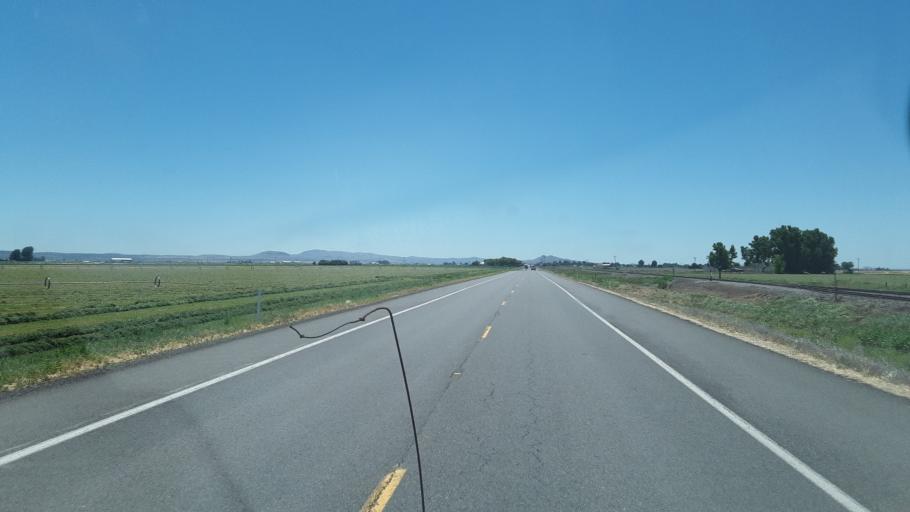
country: US
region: California
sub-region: Siskiyou County
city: Tulelake
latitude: 41.9839
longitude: -121.5038
